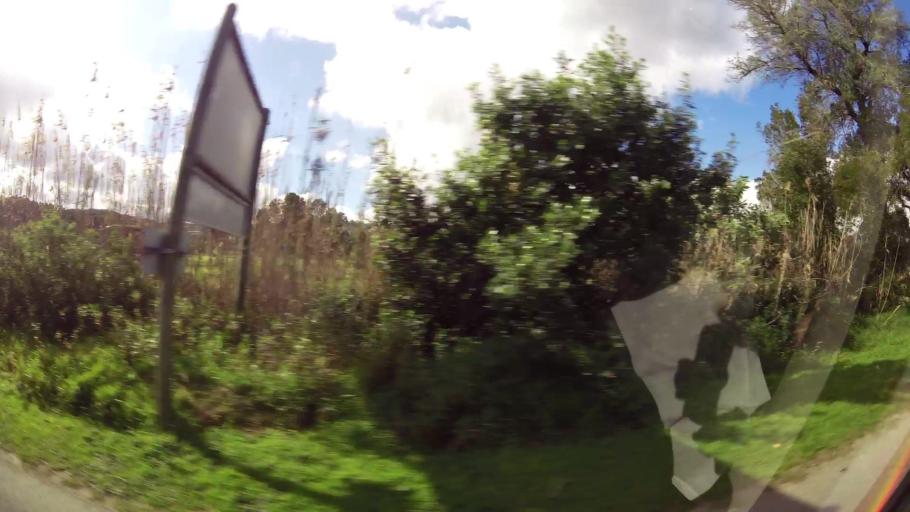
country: ZA
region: Western Cape
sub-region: Eden District Municipality
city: Knysna
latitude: -34.0518
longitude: 23.0699
